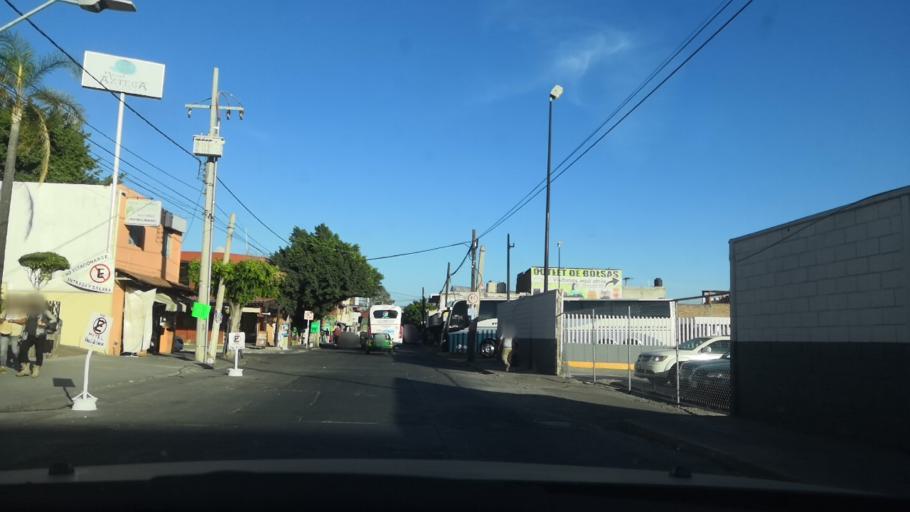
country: MX
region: Guanajuato
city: Leon
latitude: 21.1220
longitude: -101.6613
